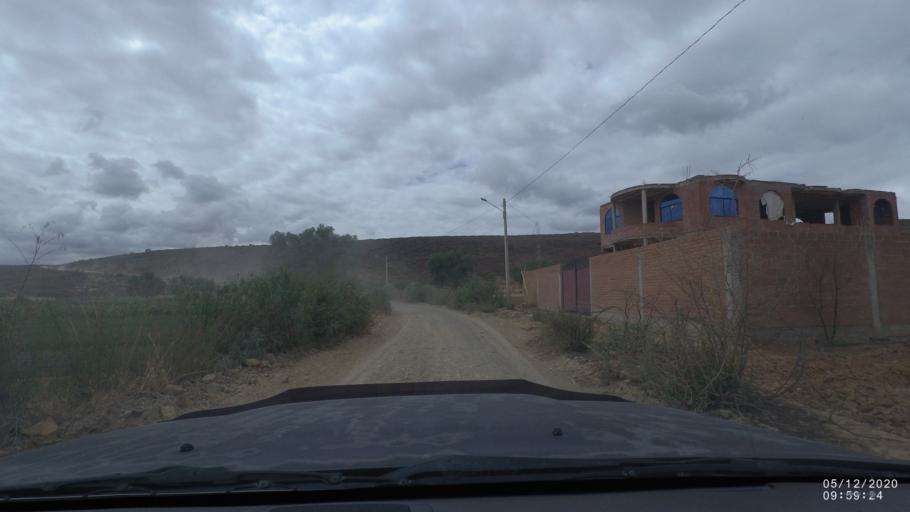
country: BO
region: Cochabamba
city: Sipe Sipe
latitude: -17.4343
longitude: -66.2916
